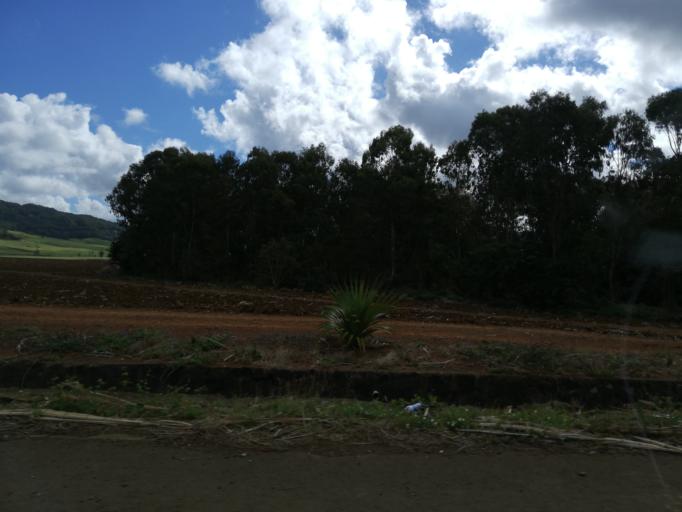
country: MU
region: Grand Port
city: Bois des Amourettes
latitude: -20.3722
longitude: 57.7005
